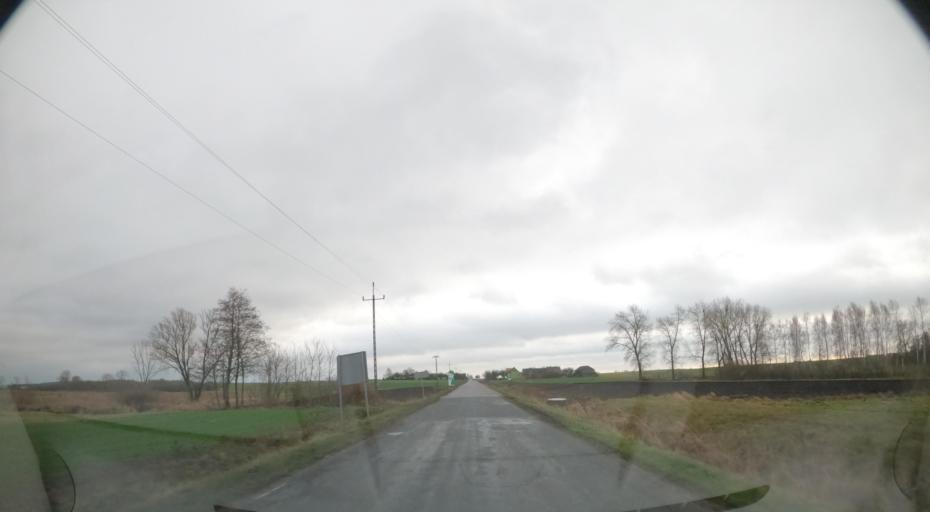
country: PL
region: Greater Poland Voivodeship
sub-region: Powiat pilski
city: Lobzenica
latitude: 53.2201
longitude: 17.3416
